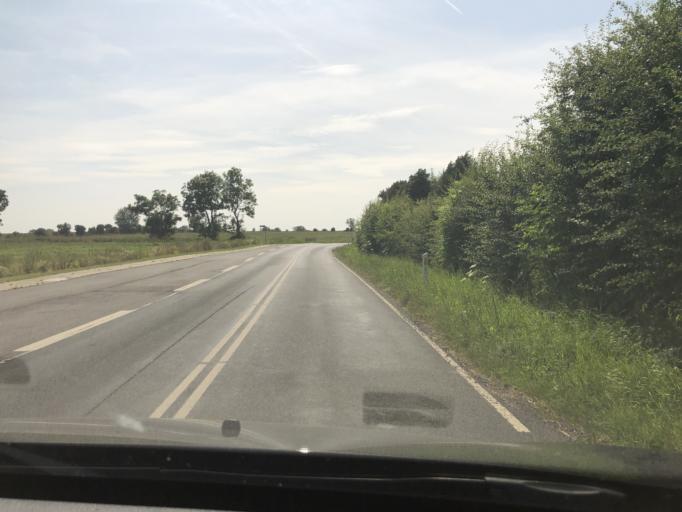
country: DK
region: South Denmark
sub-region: AEro Kommune
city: AEroskobing
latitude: 54.8708
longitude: 10.3925
